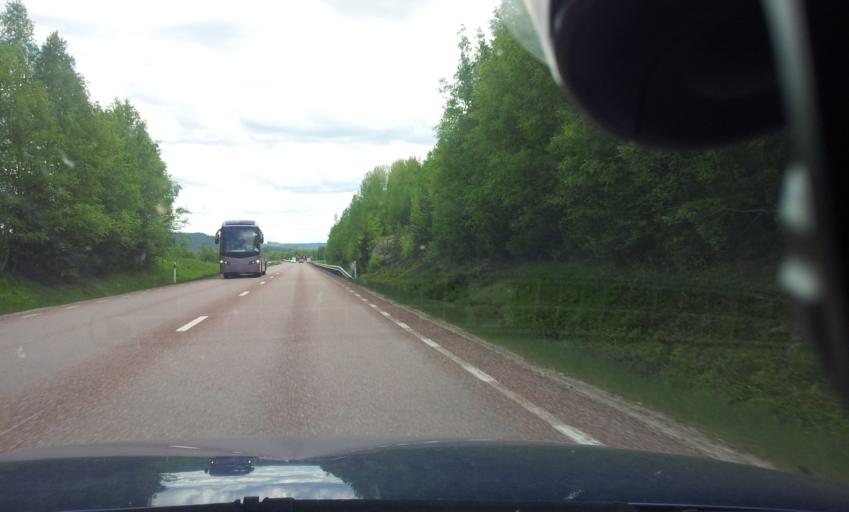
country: SE
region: Gaevleborg
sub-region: Ljusdals Kommun
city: Jaervsoe
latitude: 61.7323
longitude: 16.1644
